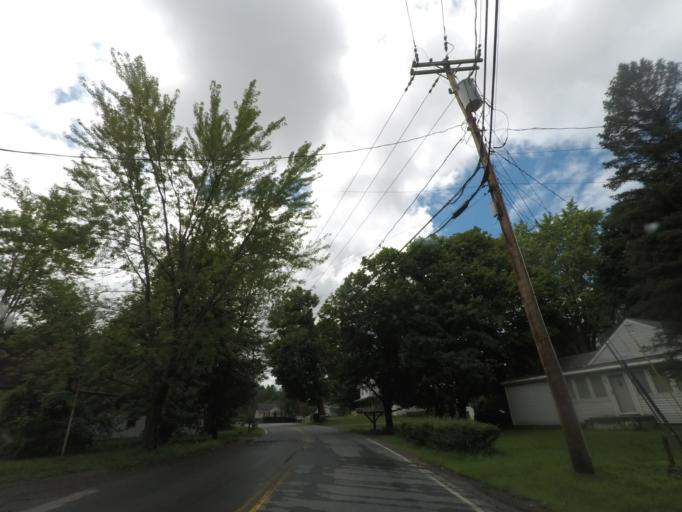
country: US
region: New York
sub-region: Rensselaer County
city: West Sand Lake
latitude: 42.6675
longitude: -73.6269
